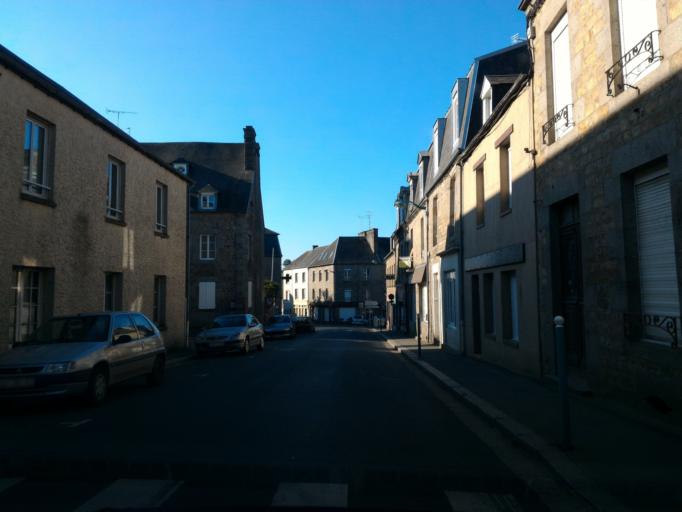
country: FR
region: Lower Normandy
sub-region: Departement de la Manche
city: La Haye-Pesnel
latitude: 48.7953
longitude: -1.3974
